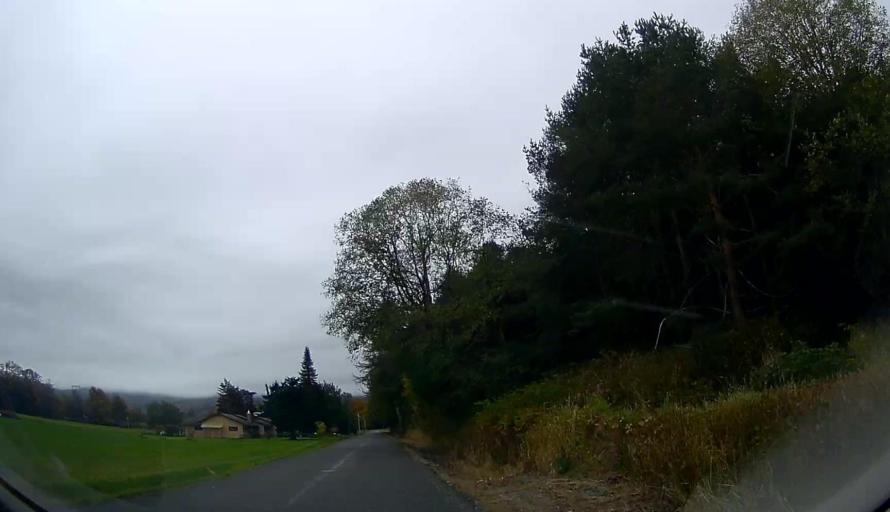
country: US
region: Washington
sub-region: Skagit County
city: Sedro-Woolley
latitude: 48.5107
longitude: -122.1721
